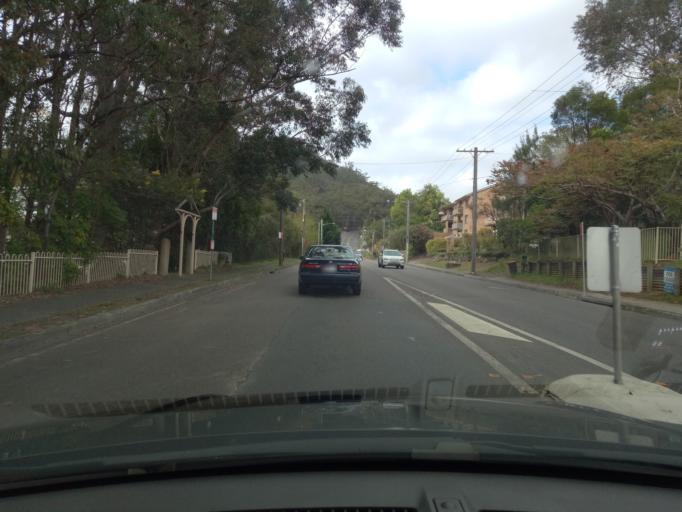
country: AU
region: New South Wales
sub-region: Gosford Shire
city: Gosford
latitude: -33.4175
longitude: 151.3487
